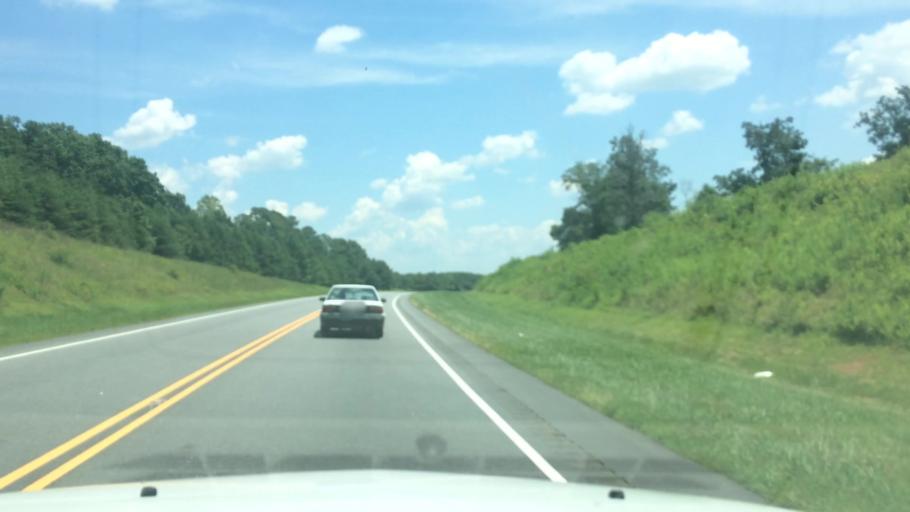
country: US
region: North Carolina
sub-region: Alexander County
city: Taylorsville
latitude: 35.9126
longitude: -81.1486
